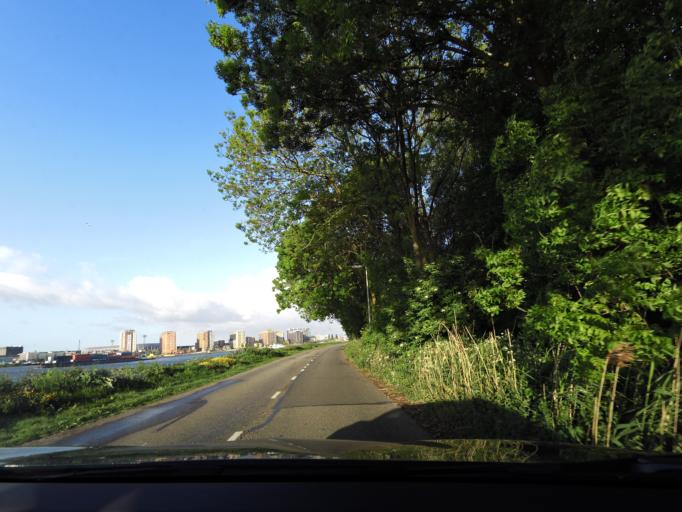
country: NL
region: South Holland
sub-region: Gemeente Rotterdam
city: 's-Gravenland
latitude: 51.9025
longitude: 4.5305
